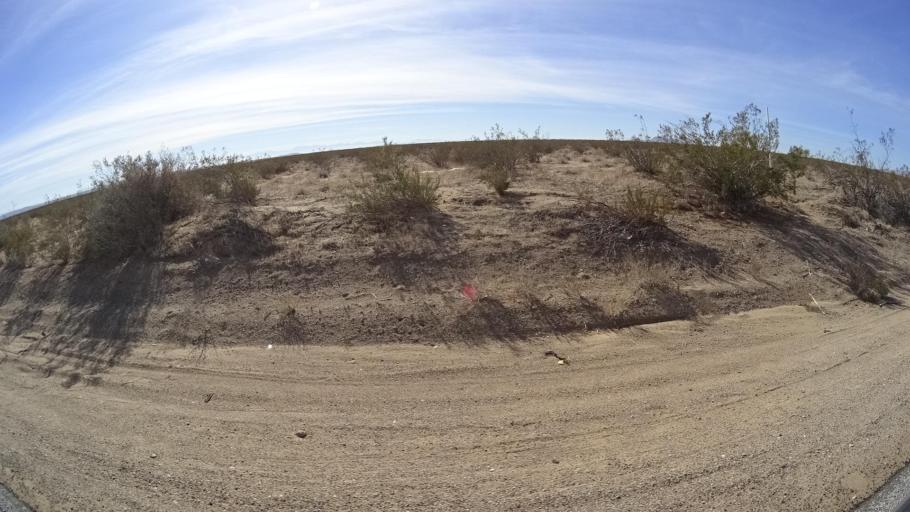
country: US
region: California
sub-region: Kern County
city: Mojave
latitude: 35.1255
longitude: -118.0959
